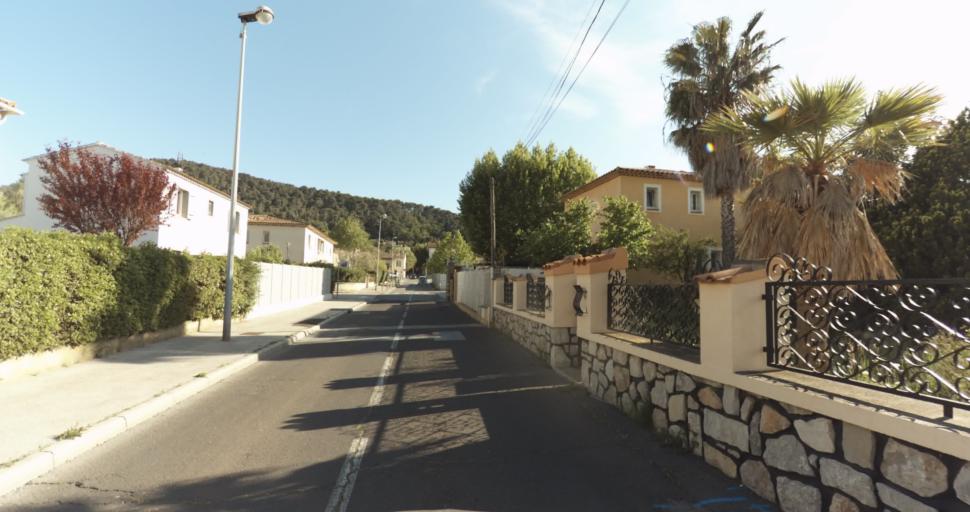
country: FR
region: Provence-Alpes-Cote d'Azur
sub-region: Departement du Var
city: Carqueiranne
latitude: 43.1215
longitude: 6.0695
